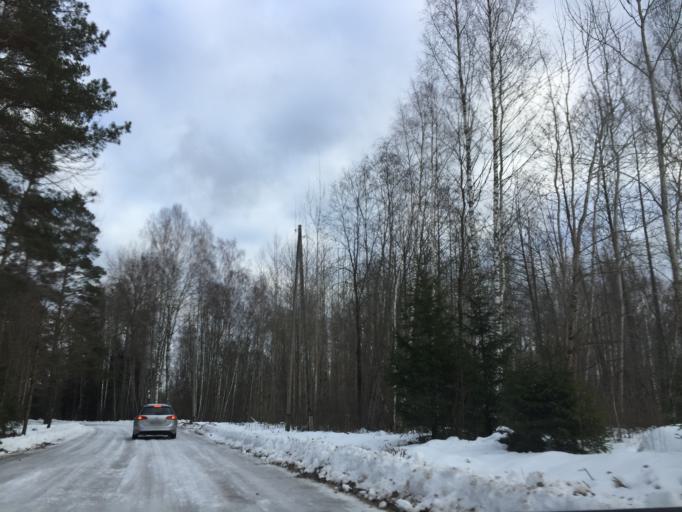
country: LV
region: Lielvarde
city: Lielvarde
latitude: 56.5799
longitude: 24.7817
